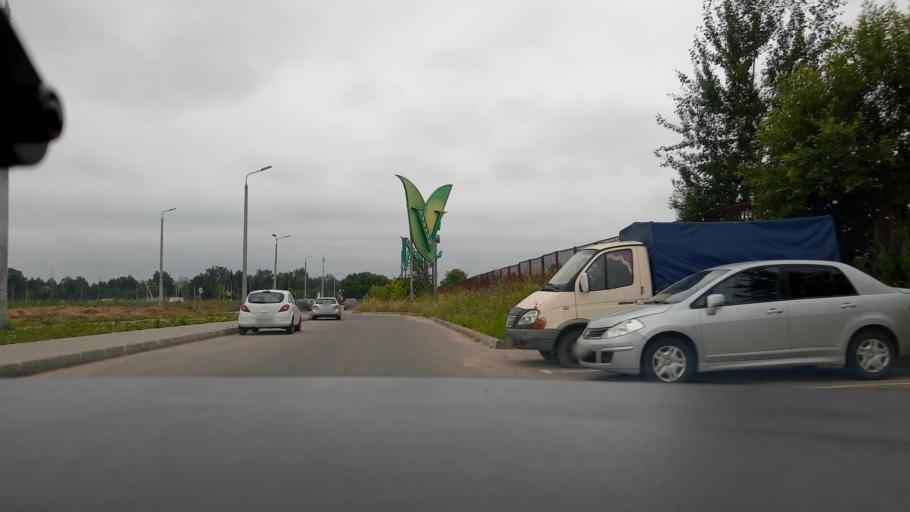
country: RU
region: Moskovskaya
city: Aprelevka
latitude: 55.5340
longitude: 37.0622
